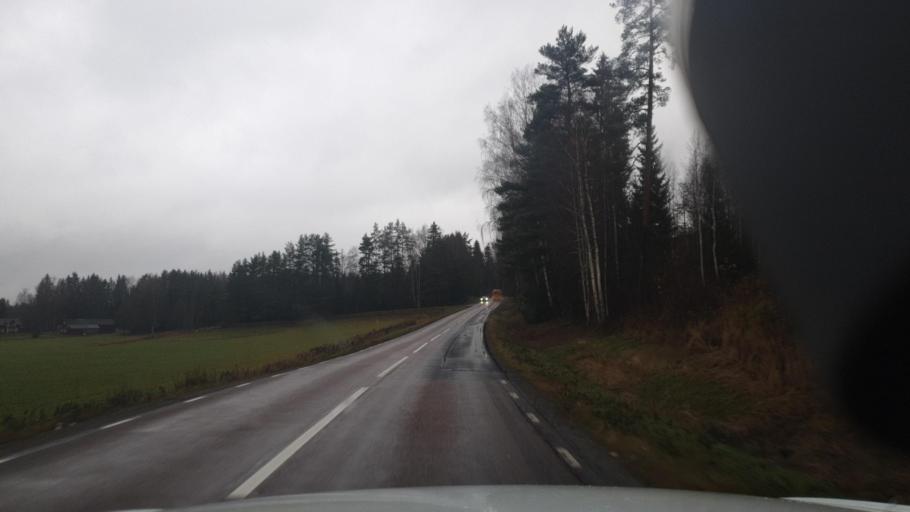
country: SE
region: Vaermland
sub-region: Eda Kommun
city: Amotfors
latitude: 59.7499
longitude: 12.2116
